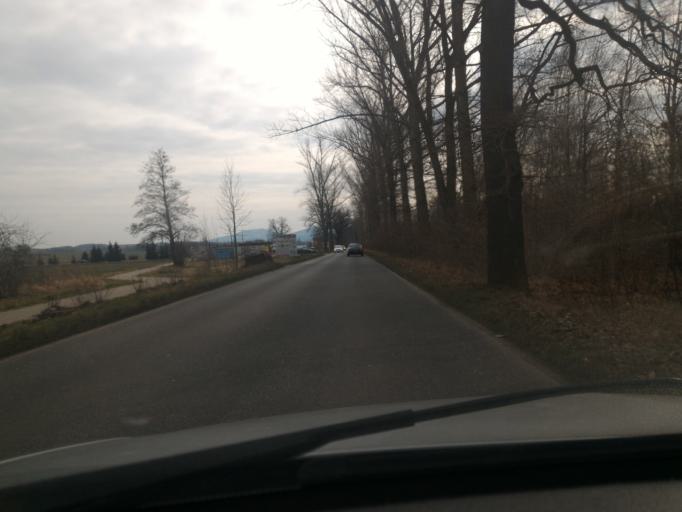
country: DE
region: Saxony
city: Zittau
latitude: 50.8806
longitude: 14.8216
